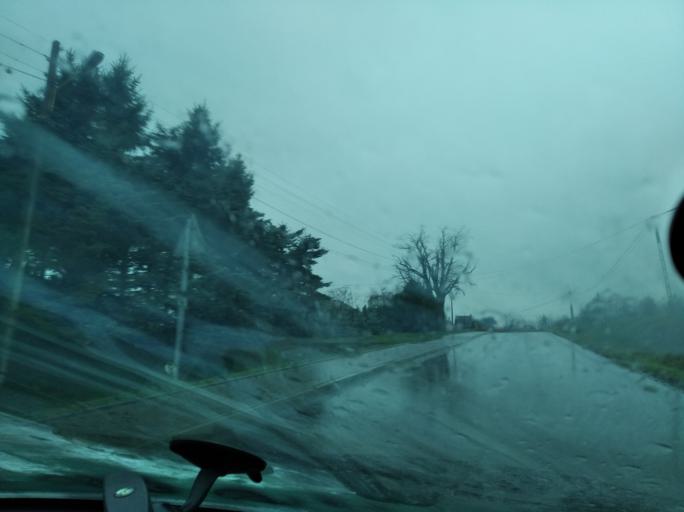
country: PL
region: Subcarpathian Voivodeship
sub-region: Powiat lancucki
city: Wysoka
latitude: 50.0433
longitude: 22.2362
